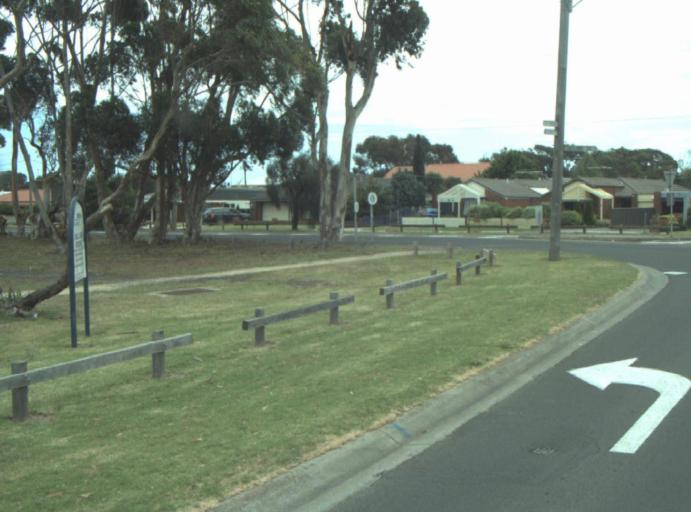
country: AU
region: Victoria
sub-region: Greater Geelong
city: Leopold
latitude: -38.2475
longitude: 144.5286
